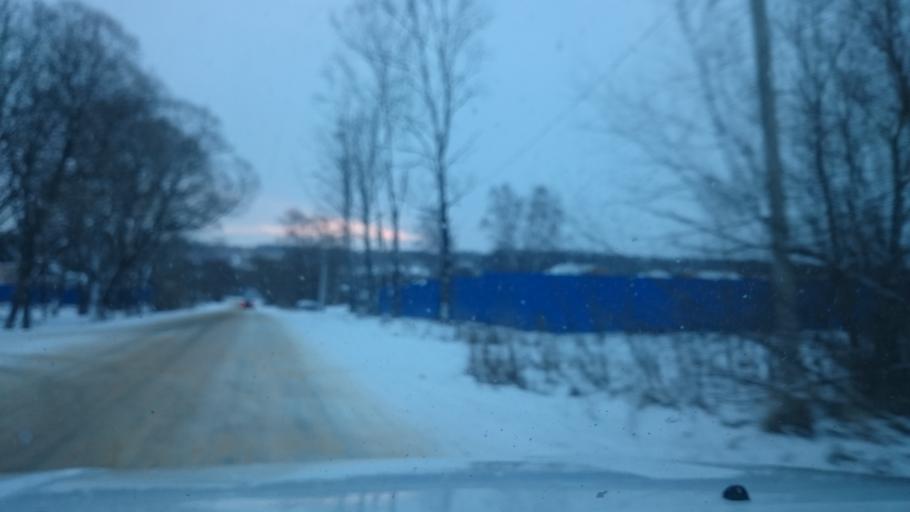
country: RU
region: Tula
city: Leninskiy
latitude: 54.2462
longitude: 37.2569
